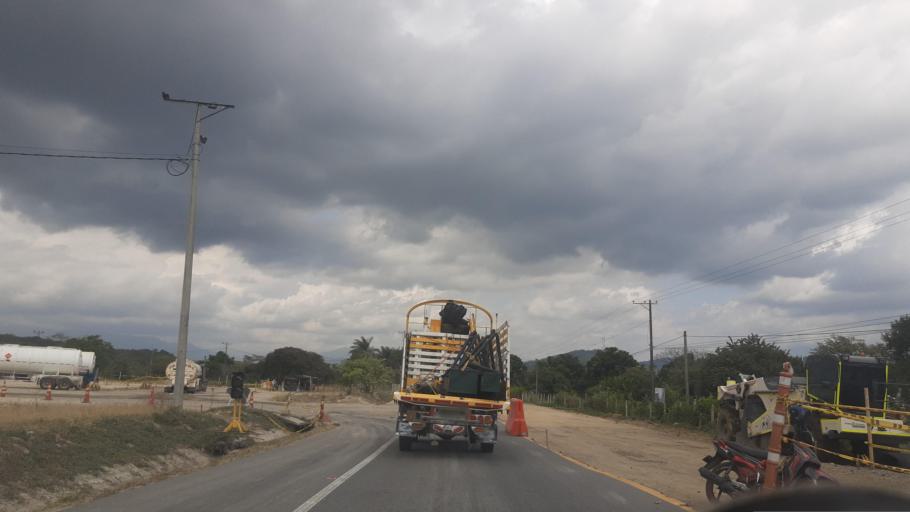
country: CO
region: Casanare
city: Tauramena
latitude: 4.9905
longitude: -72.6850
